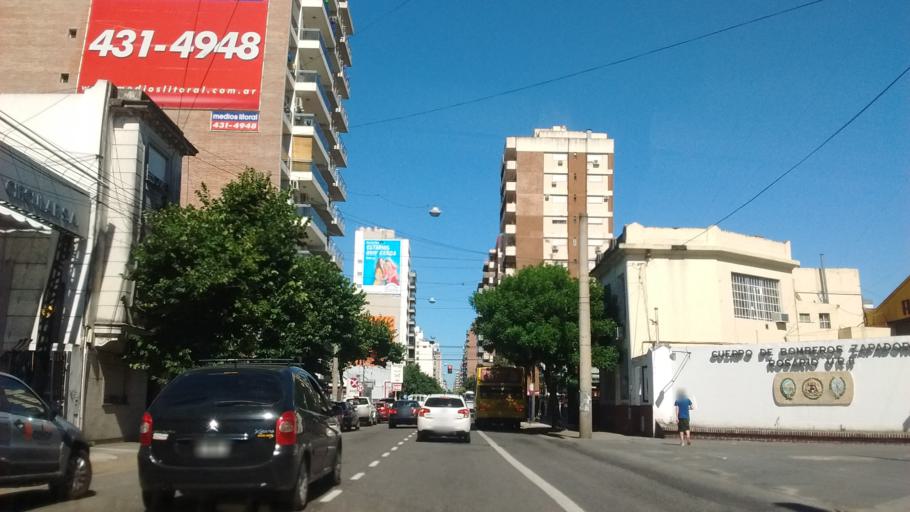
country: AR
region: Santa Fe
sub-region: Departamento de Rosario
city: Rosario
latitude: -32.9421
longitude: -60.6624
